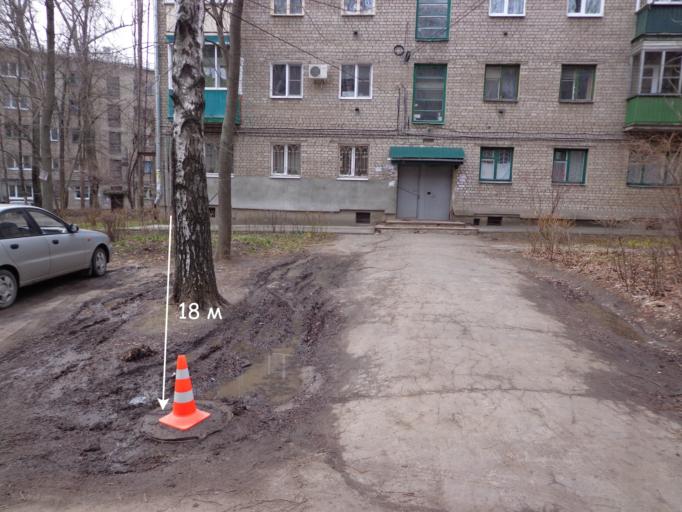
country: RU
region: Voronezj
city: Voronezh
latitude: 51.7013
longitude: 39.2240
